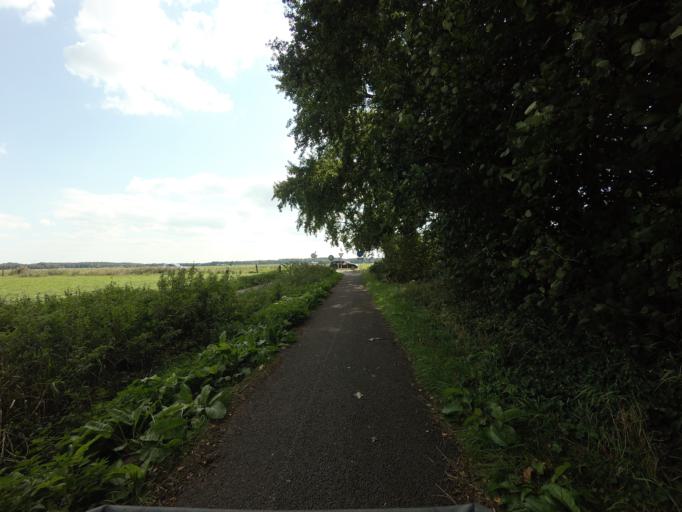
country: NL
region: Drenthe
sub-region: Gemeente Westerveld
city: Dwingeloo
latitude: 52.8500
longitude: 6.4668
